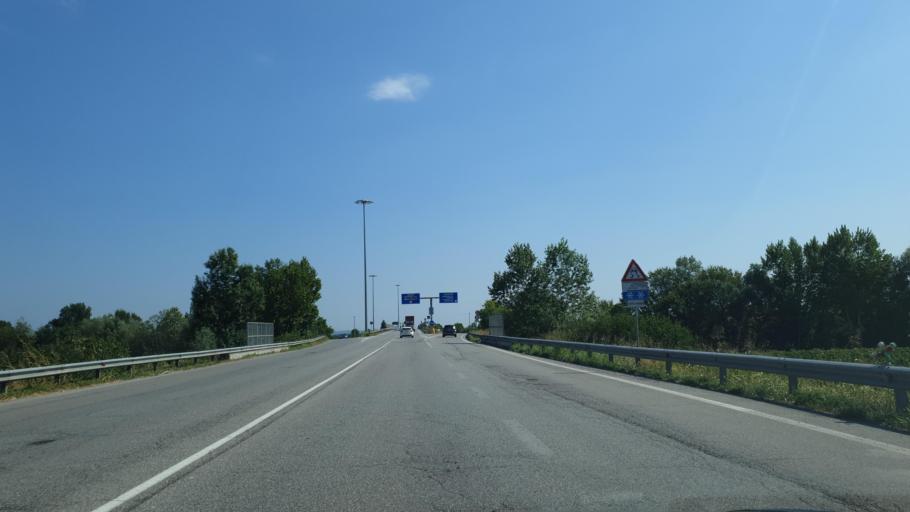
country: IT
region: Lombardy
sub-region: Provincia di Brescia
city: San Martino della Battaglia
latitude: 45.4452
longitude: 10.5912
